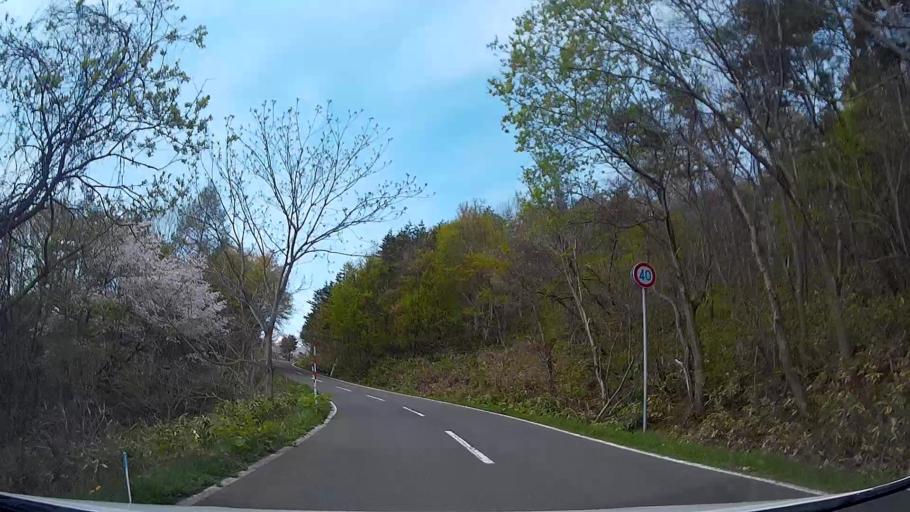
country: JP
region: Iwate
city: Shizukuishi
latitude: 39.9255
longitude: 140.9733
